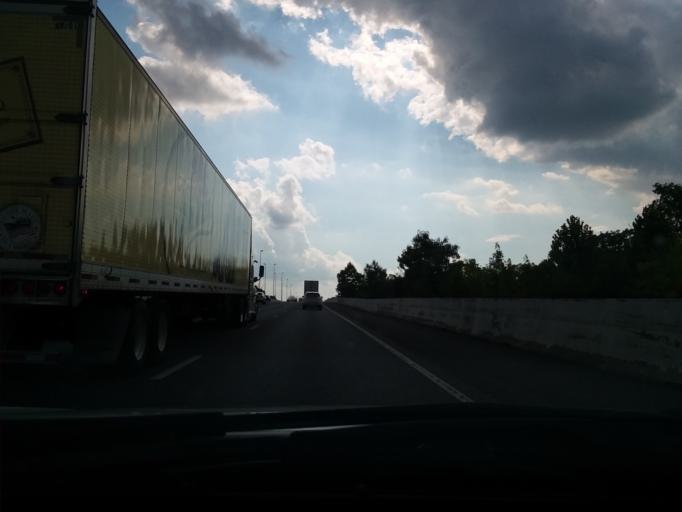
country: US
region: Tennessee
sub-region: Davidson County
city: Lakewood
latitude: 36.2359
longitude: -86.7088
